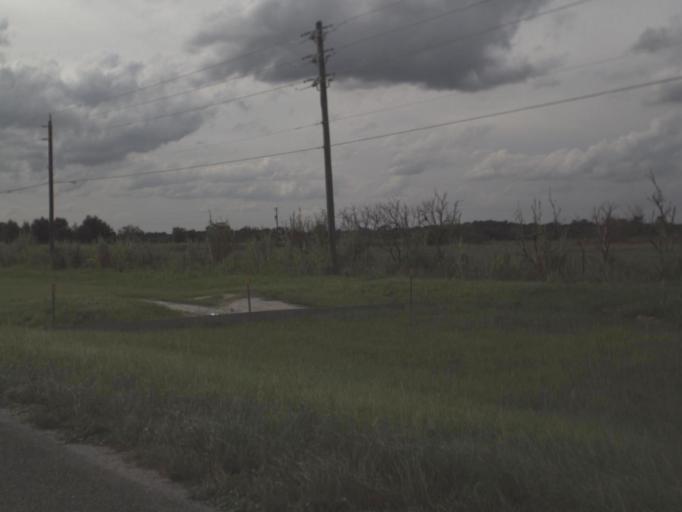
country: US
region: Florida
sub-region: Lee County
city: Alva
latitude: 26.7098
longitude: -81.5564
